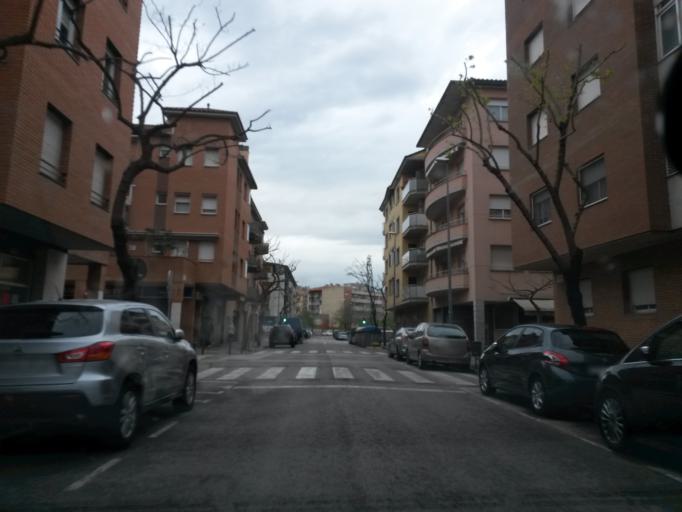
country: ES
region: Catalonia
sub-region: Provincia de Girona
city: Salt
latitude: 41.9737
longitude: 2.8062
